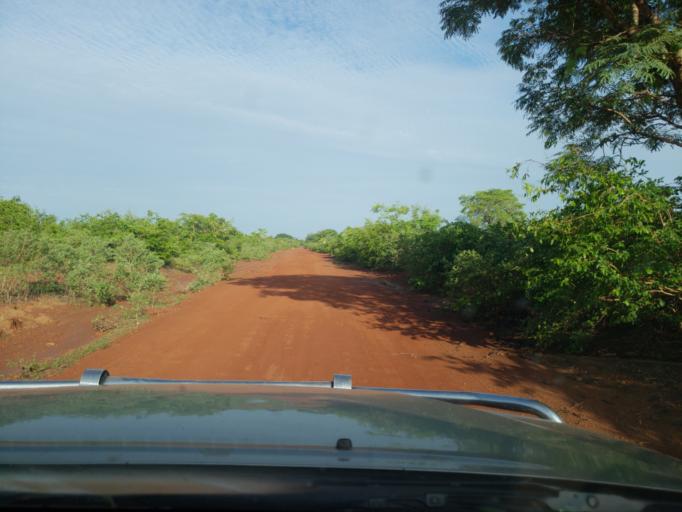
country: ML
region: Sikasso
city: Koutiala
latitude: 12.4251
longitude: -5.6538
